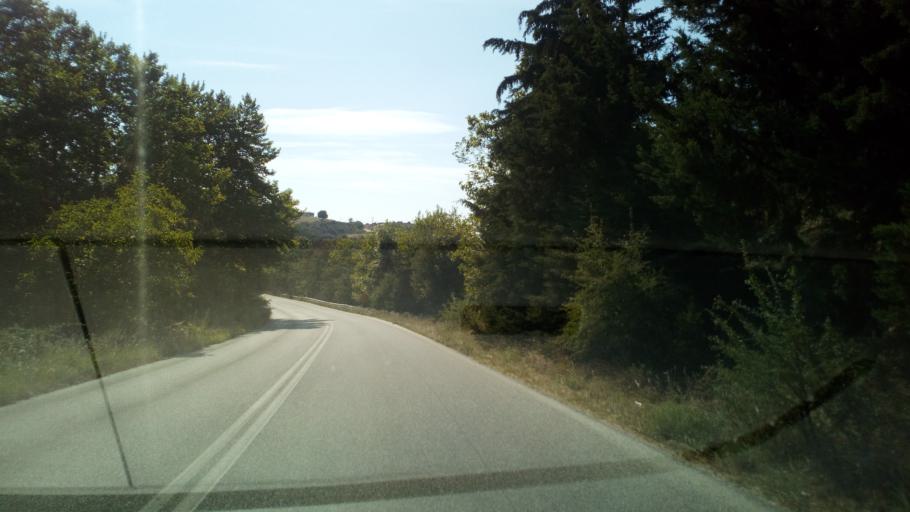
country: GR
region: Central Macedonia
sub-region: Nomos Chalkidikis
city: Arnaia
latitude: 40.5044
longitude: 23.4818
